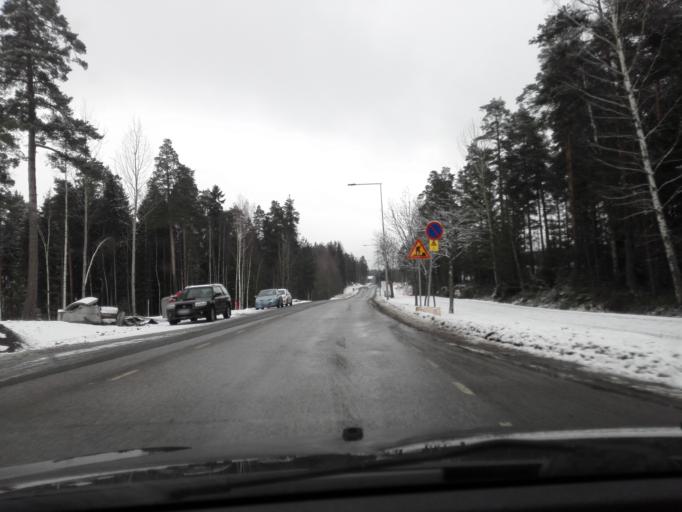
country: FI
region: Uusimaa
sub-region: Helsinki
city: Vantaa
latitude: 60.2853
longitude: 25.0689
